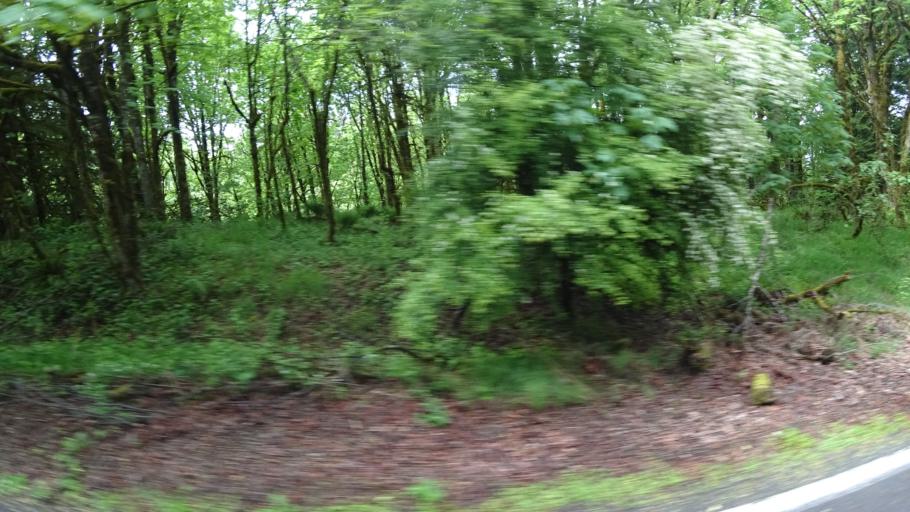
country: US
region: Oregon
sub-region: Washington County
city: West Haven
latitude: 45.5436
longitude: -122.7590
